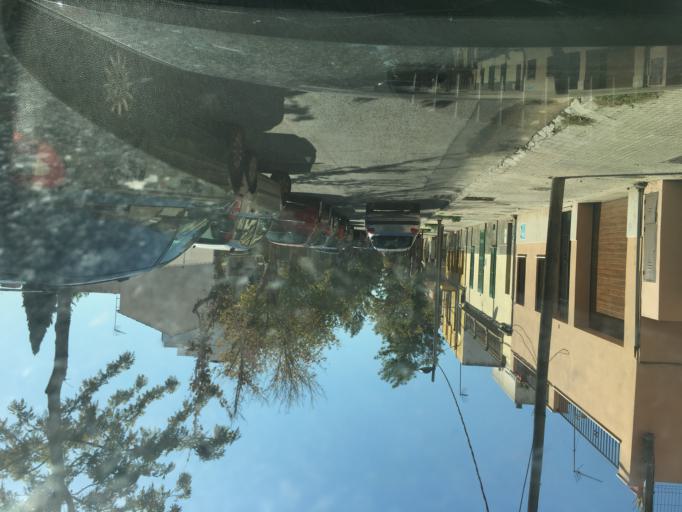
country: ES
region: Balearic Islands
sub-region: Illes Balears
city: Palma
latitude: 39.5856
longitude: 2.6742
